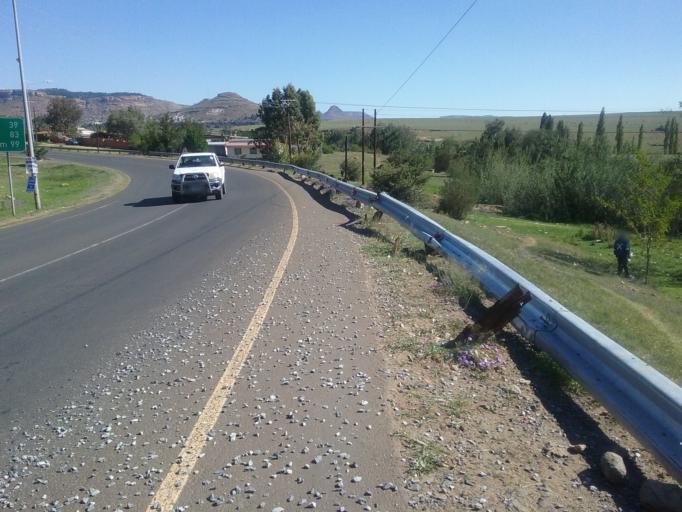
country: LS
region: Maseru
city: Maseru
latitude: -29.3076
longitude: 27.4651
